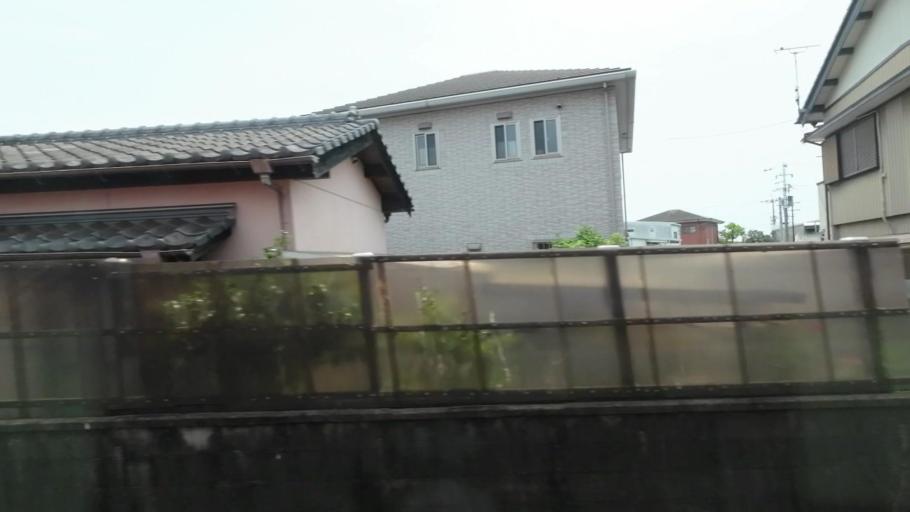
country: JP
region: Kochi
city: Kochi-shi
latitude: 33.6037
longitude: 133.6762
